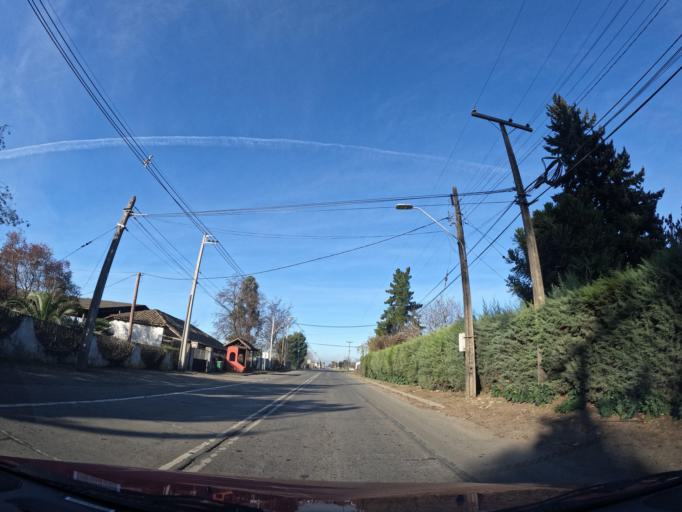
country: CL
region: Maule
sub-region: Provincia de Linares
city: San Javier
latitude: -35.5730
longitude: -71.6805
